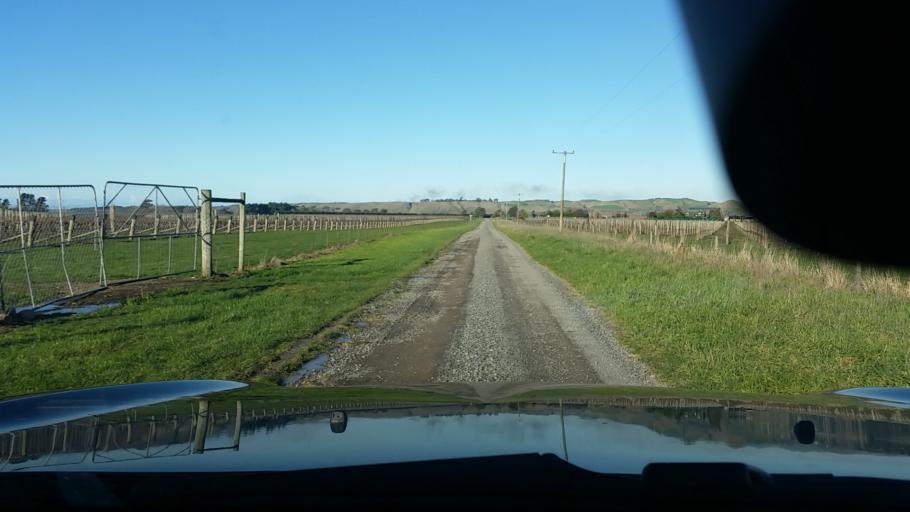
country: NZ
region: Marlborough
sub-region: Marlborough District
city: Blenheim
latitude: -41.6420
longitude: 174.0413
